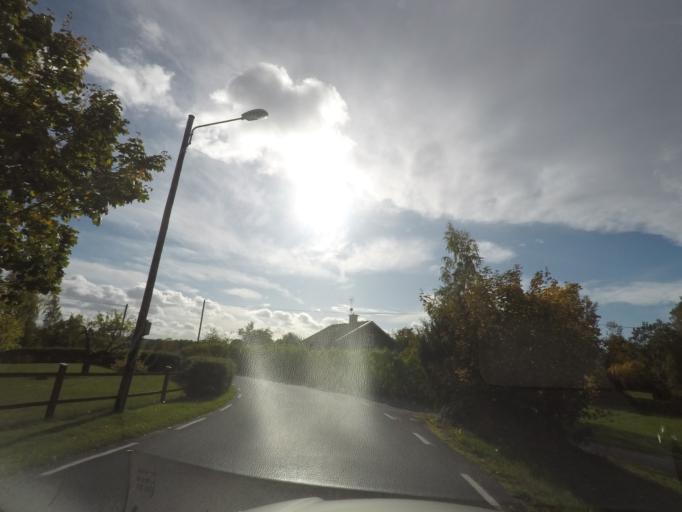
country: SE
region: Soedermanland
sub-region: Eskilstuna Kommun
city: Kvicksund
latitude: 59.3192
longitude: 16.2476
